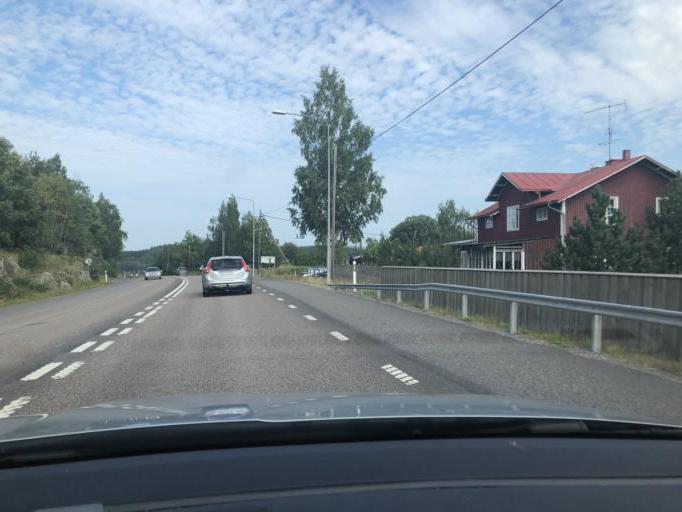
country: SE
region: Vaesternorrland
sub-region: Kramfors Kommun
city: Kramfors
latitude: 62.8889
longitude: 17.8526
